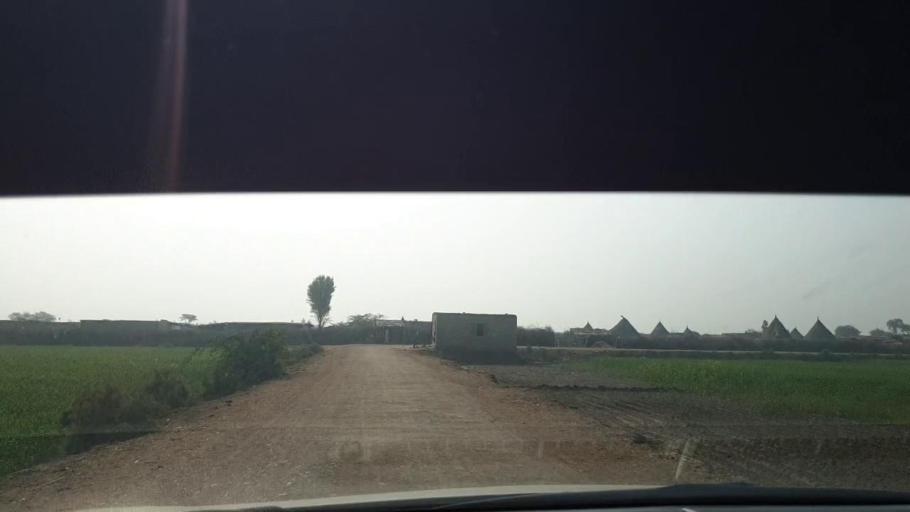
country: PK
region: Sindh
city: Berani
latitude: 25.7713
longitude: 68.8007
